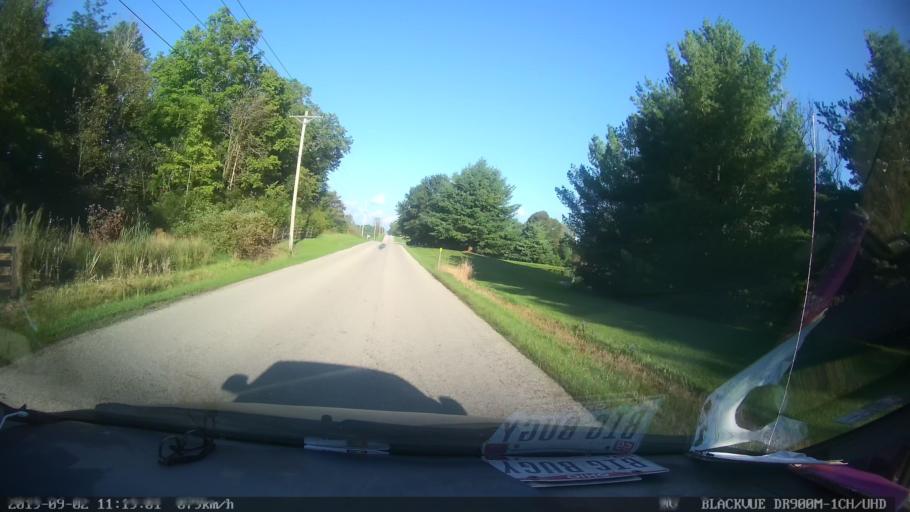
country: US
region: Ohio
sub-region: Morrow County
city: Mount Gilead
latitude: 40.5153
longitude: -82.7644
